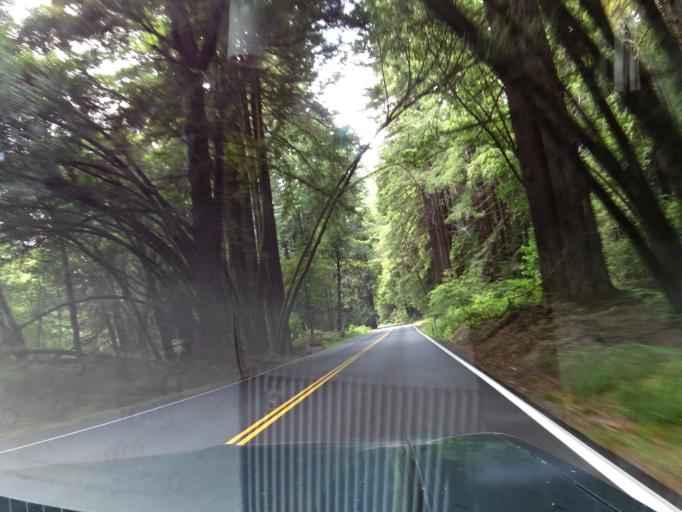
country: US
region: California
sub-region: Mendocino County
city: Fort Bragg
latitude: 39.1764
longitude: -123.6780
